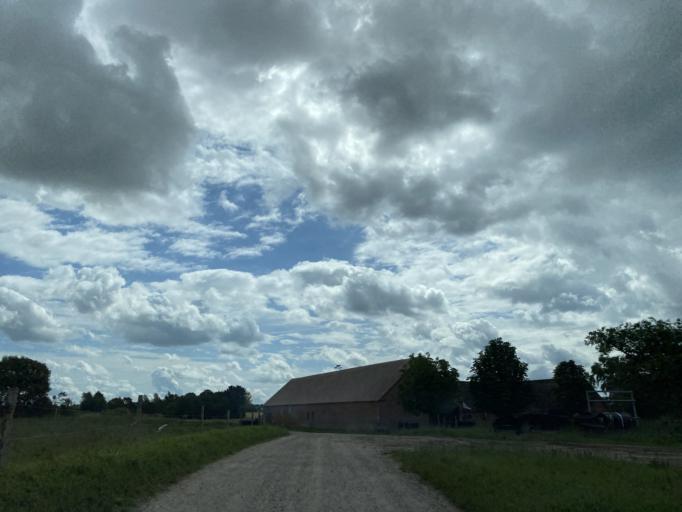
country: DK
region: Central Jutland
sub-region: Silkeborg Kommune
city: Silkeborg
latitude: 56.2213
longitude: 9.5652
